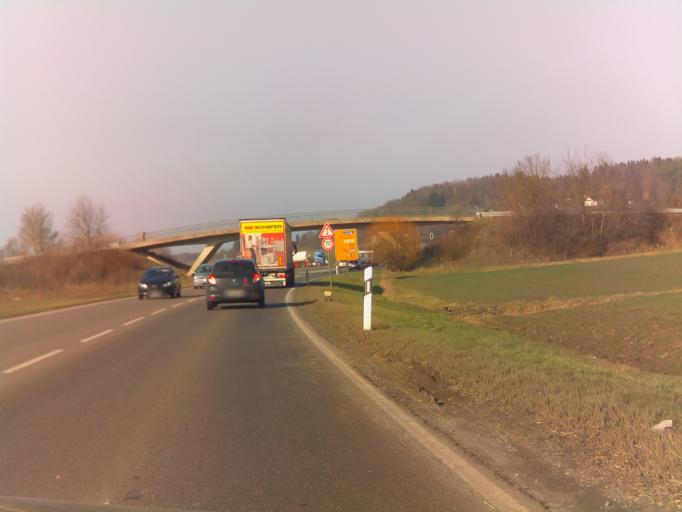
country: DE
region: Baden-Wuerttemberg
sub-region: Regierungsbezirk Stuttgart
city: Renningen
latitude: 48.7655
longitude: 8.9478
